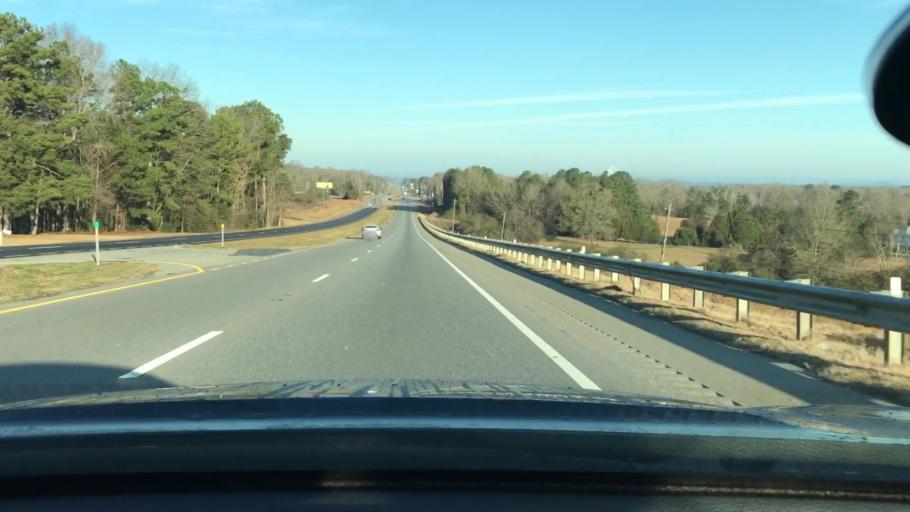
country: US
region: Alabama
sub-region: Talladega County
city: Mignon
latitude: 33.2061
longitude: -86.3089
